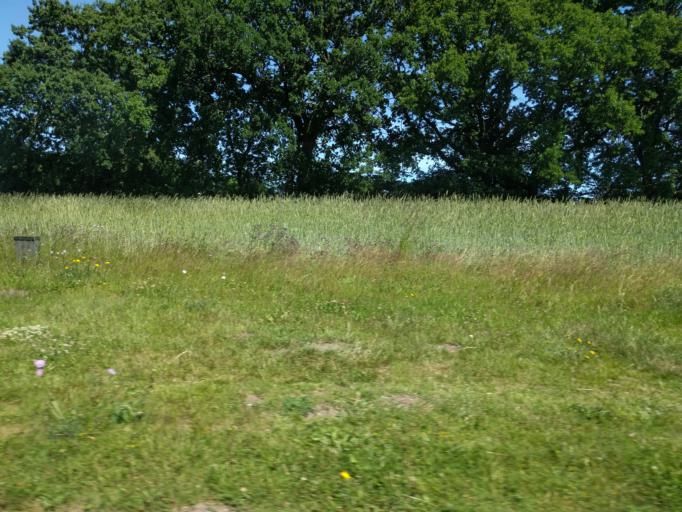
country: DK
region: South Denmark
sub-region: Kerteminde Kommune
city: Langeskov
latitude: 55.3482
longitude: 10.5767
